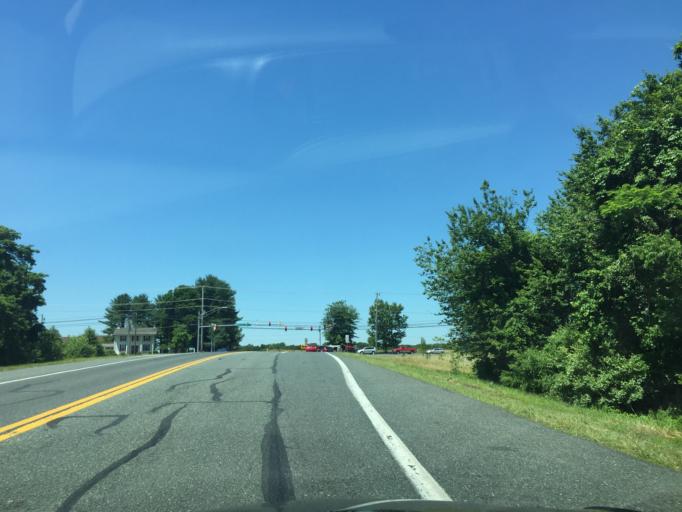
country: US
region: Maryland
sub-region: Harford County
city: Jarrettsville
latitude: 39.5869
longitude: -76.4712
